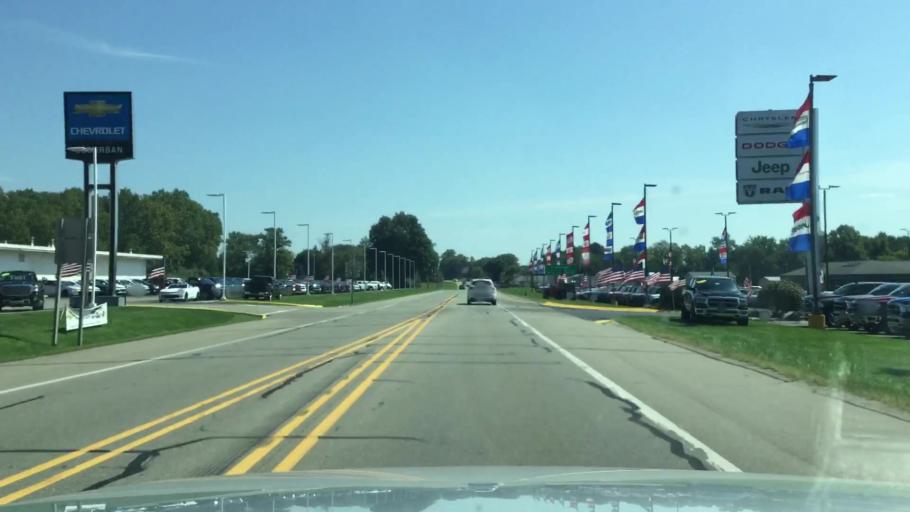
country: US
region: Michigan
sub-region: Lenawee County
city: Clinton
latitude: 42.0714
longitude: -84.0117
